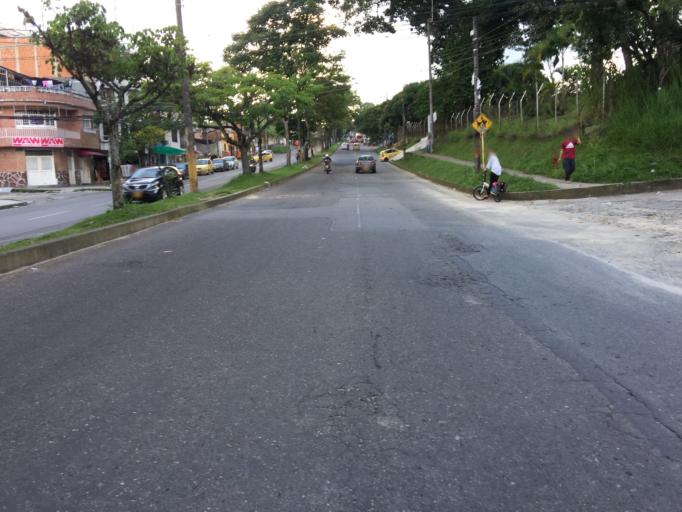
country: CO
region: Tolima
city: Ibague
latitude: 4.4460
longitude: -75.2157
